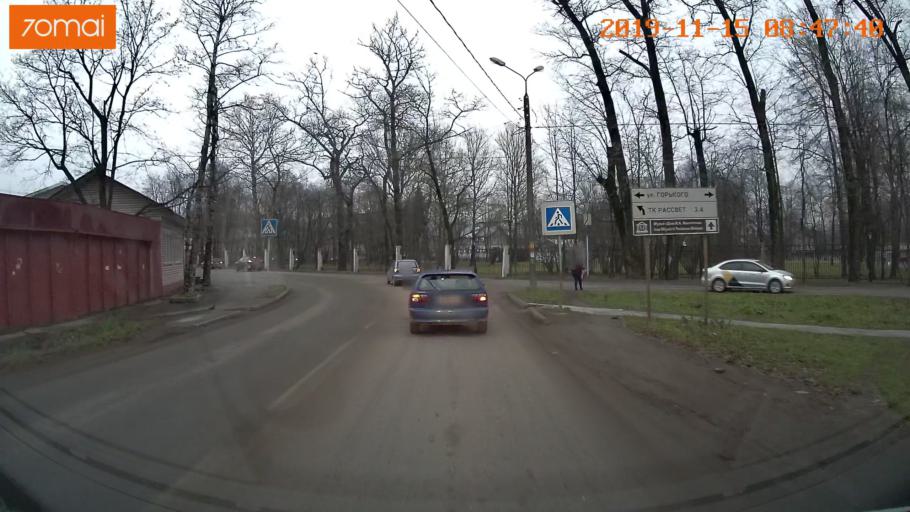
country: RU
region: Vologda
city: Cherepovets
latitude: 59.1213
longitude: 37.9176
